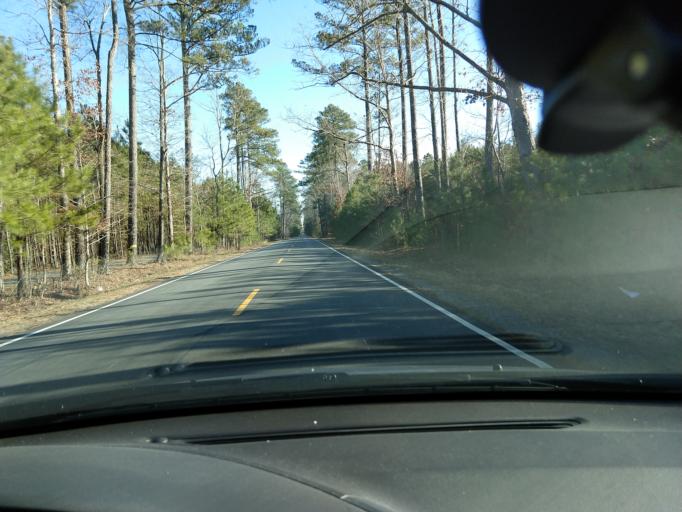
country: US
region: Virginia
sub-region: Charles City County
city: Charles City
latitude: 37.2829
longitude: -76.9201
